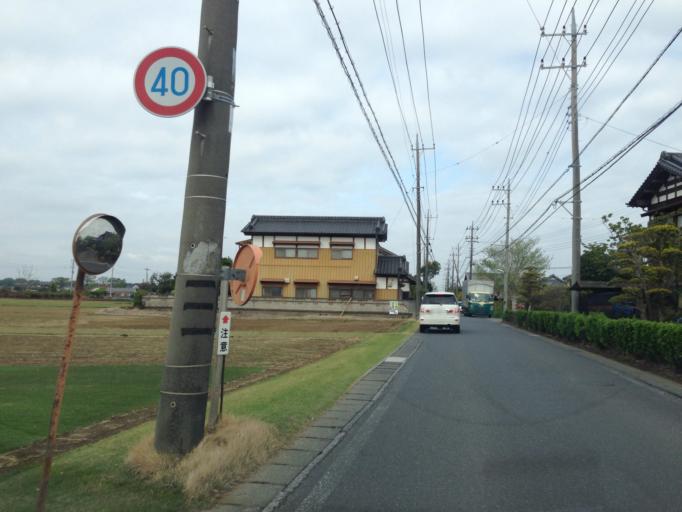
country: JP
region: Ibaraki
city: Ishige
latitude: 36.1422
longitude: 140.0402
